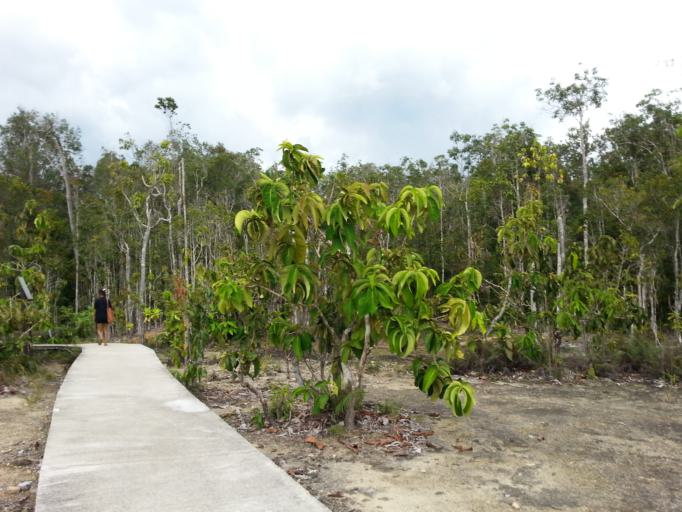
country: TH
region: Krabi
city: Khlong Thom
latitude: 7.9256
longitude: 99.2688
